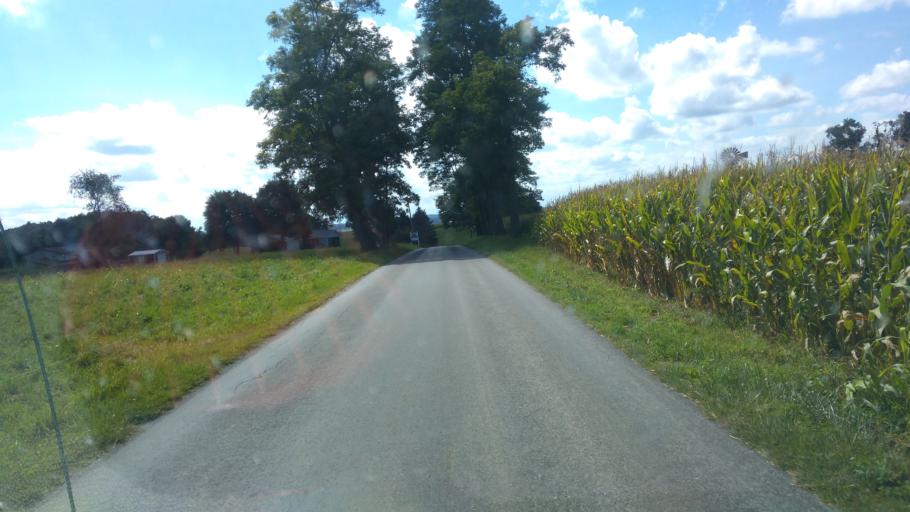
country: US
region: Ohio
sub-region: Holmes County
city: Millersburg
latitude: 40.6191
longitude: -81.8403
